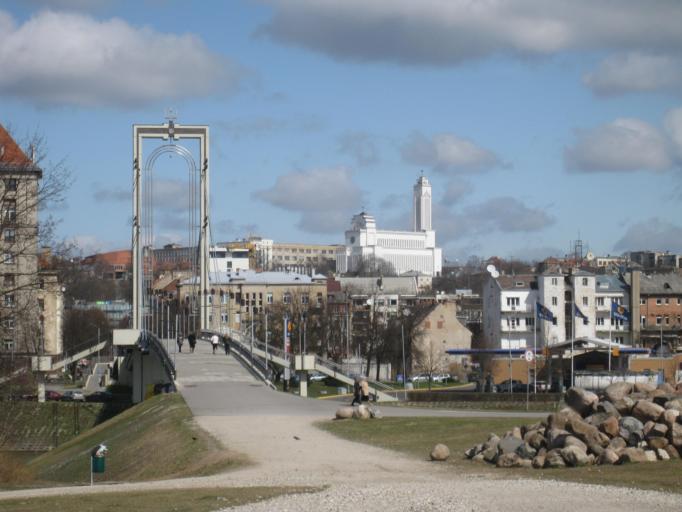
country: LT
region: Kauno apskritis
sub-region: Kaunas
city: Kaunas
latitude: 54.8925
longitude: 23.9130
